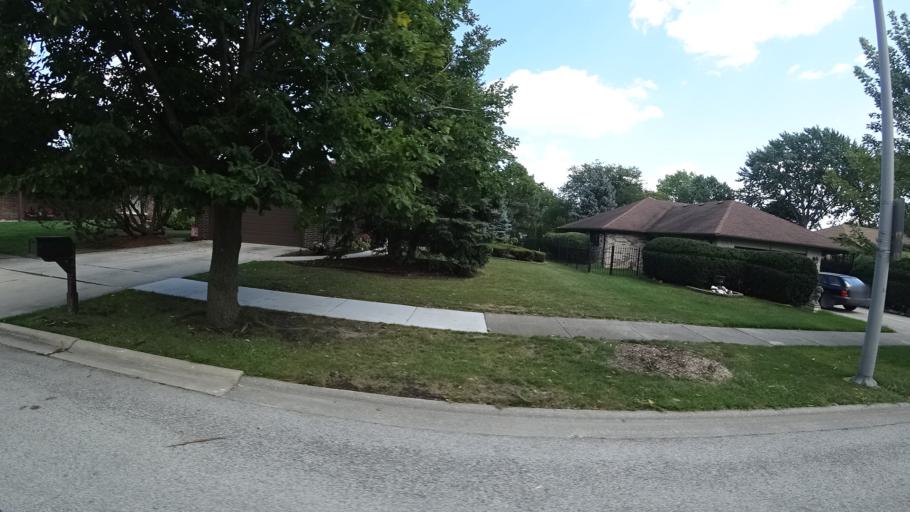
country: US
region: Illinois
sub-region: Cook County
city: Orland Park
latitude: 41.6287
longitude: -87.8239
